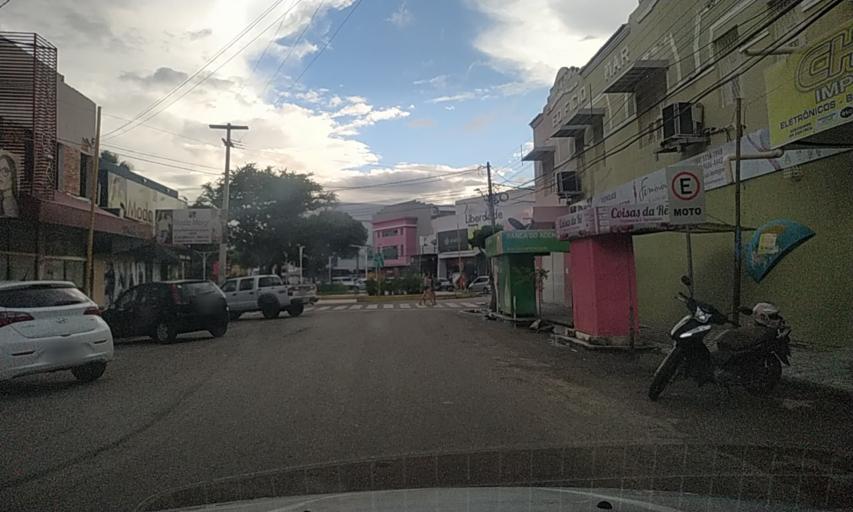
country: BR
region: Rio Grande do Norte
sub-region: Mossoro
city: Mossoro
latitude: -5.1930
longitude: -37.3427
